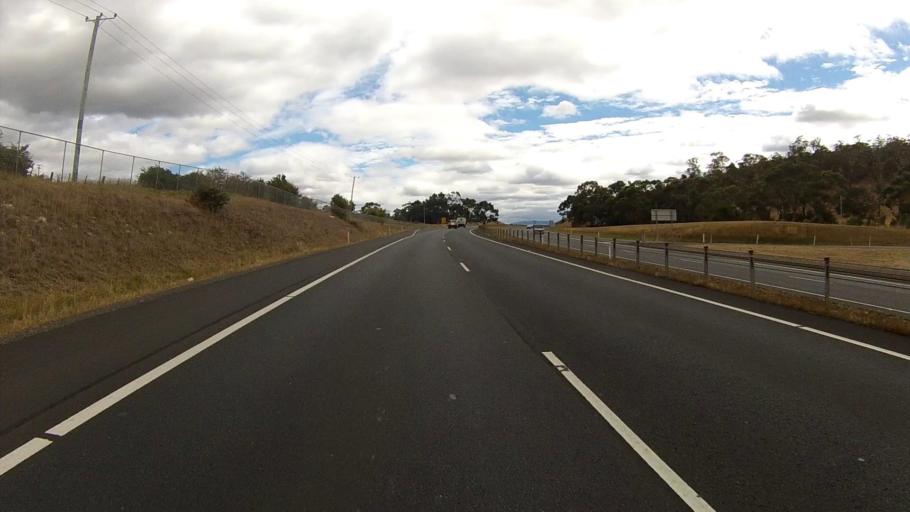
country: AU
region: Tasmania
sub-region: Glenorchy
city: Claremont
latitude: -42.7797
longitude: 147.2382
